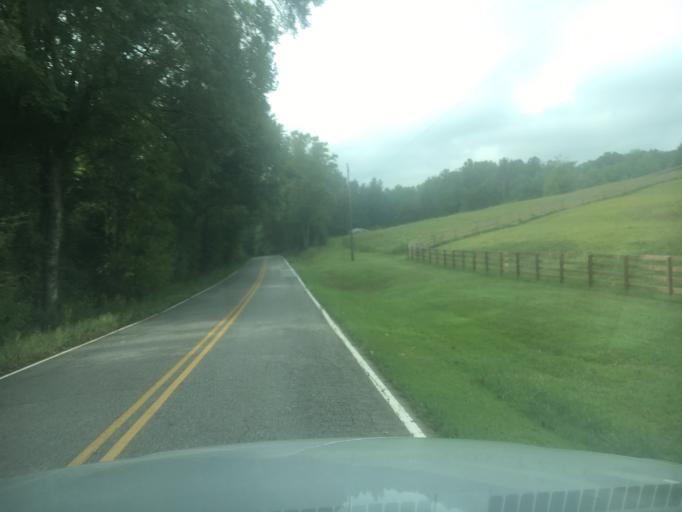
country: US
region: South Carolina
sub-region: Spartanburg County
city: Inman
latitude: 35.1836
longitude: -82.0458
